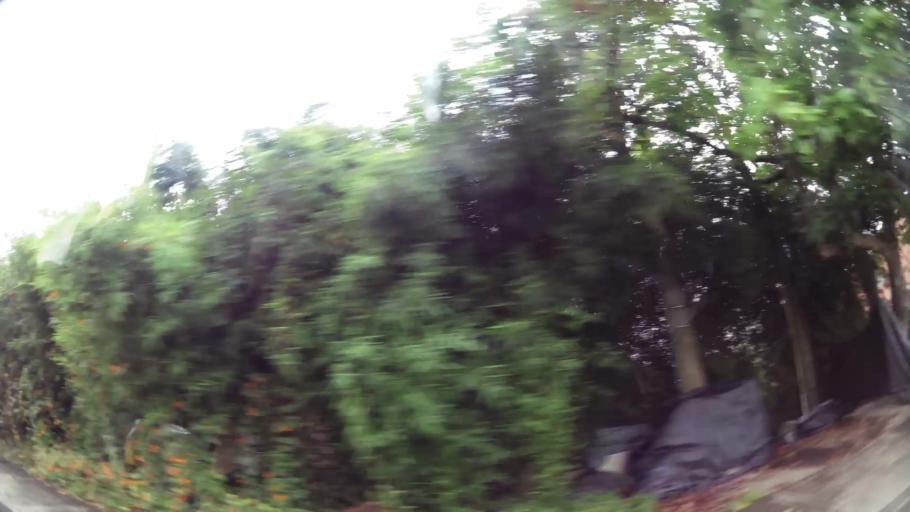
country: CO
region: Antioquia
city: Envigado
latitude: 6.1921
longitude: -75.5567
